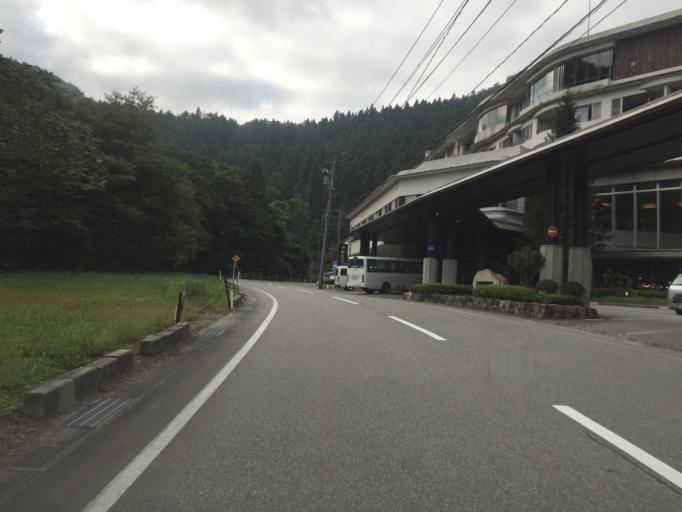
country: JP
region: Fukushima
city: Inawashiro
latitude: 37.4686
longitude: 139.9628
